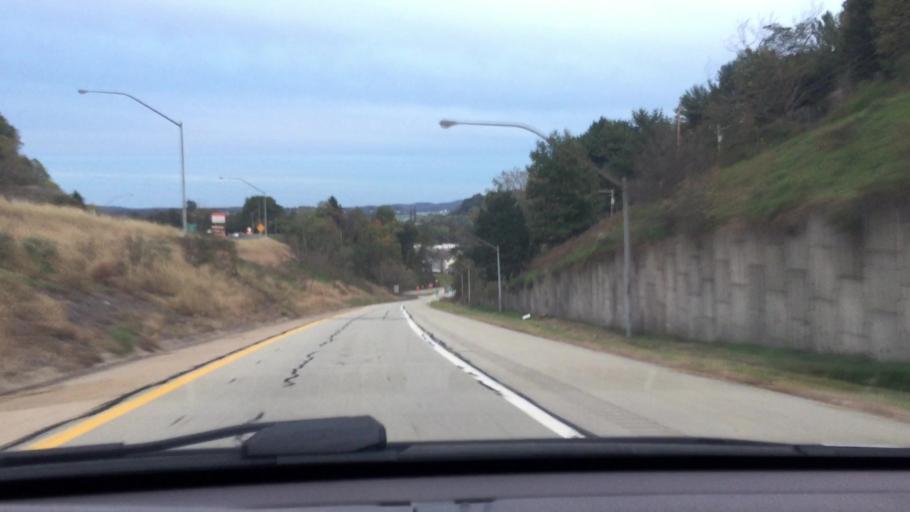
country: US
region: Pennsylvania
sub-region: Westmoreland County
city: Arnold
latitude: 40.5805
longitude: -79.7830
